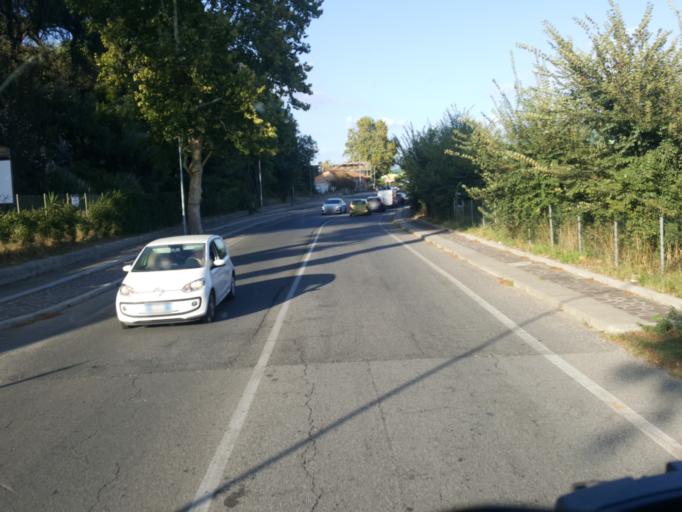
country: IT
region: Latium
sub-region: Citta metropolitana di Roma Capitale
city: Girardi-Bellavista-Terrazze
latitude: 42.0992
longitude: 12.5791
